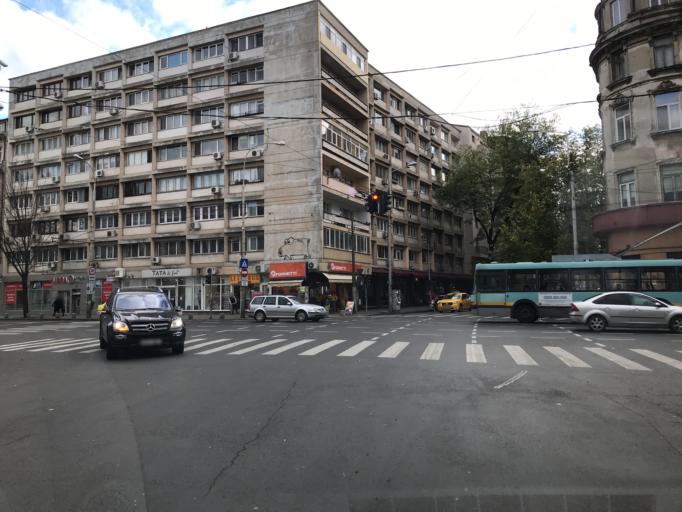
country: RO
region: Bucuresti
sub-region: Municipiul Bucuresti
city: Bucuresti
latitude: 44.4348
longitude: 26.0897
